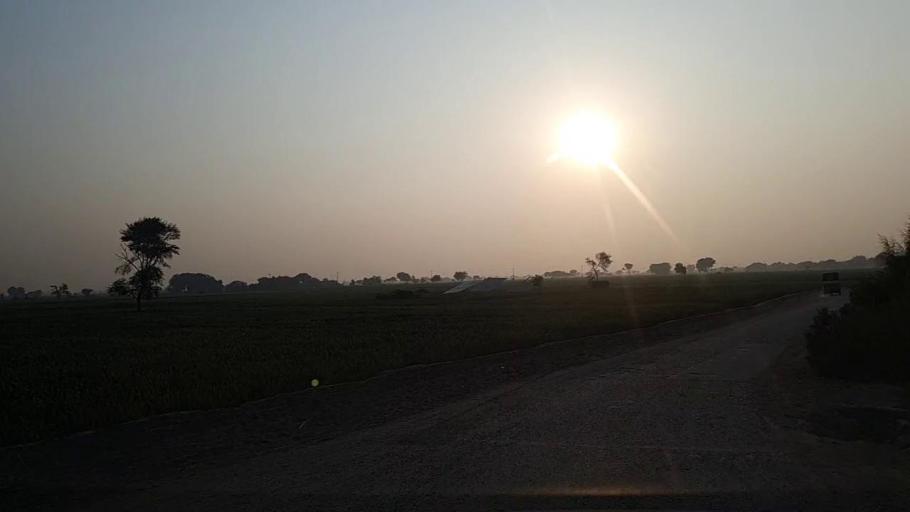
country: PK
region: Sindh
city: Sann
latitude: 26.1949
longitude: 68.0890
